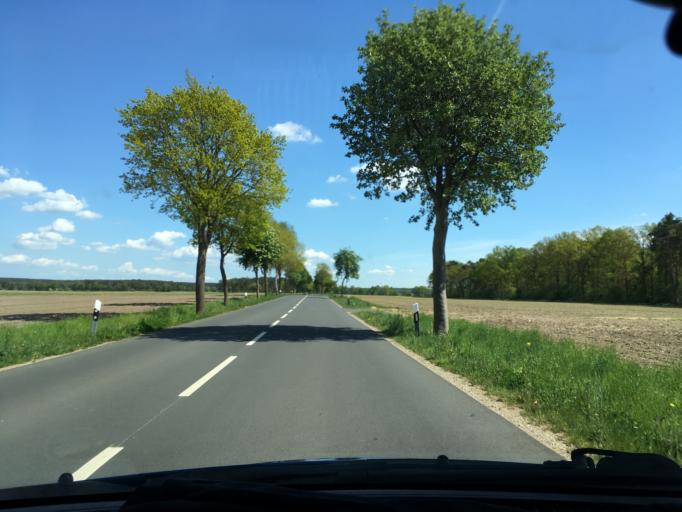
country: DE
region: Lower Saxony
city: Himbergen
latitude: 53.0806
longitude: 10.7502
